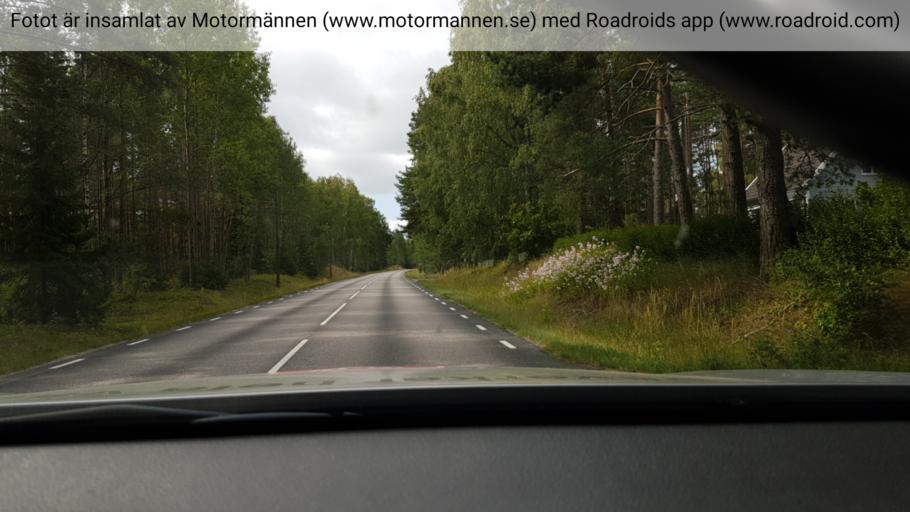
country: SE
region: Stockholm
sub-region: Norrtalje Kommun
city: Rimbo
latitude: 59.7054
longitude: 18.4150
